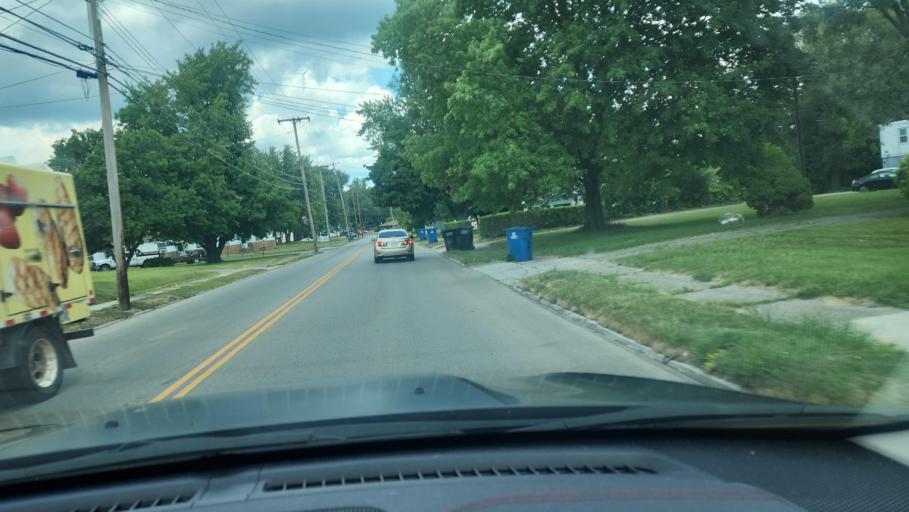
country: US
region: Ohio
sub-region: Mahoning County
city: Struthers
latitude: 41.0447
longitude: -80.5930
